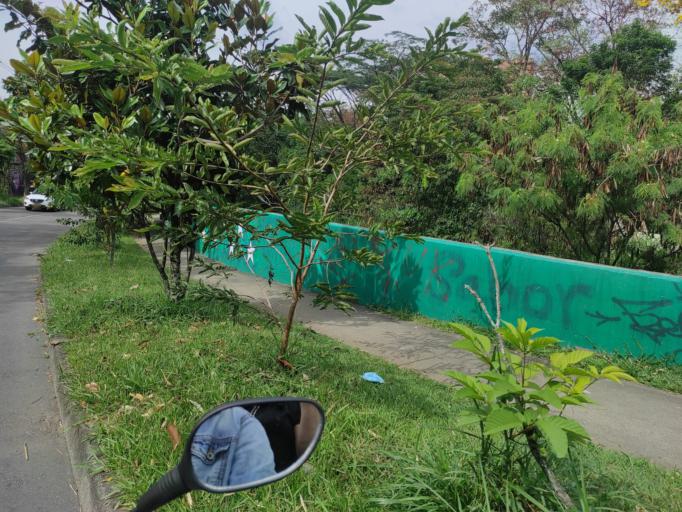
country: CO
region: Antioquia
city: Envigado
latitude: 6.1618
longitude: -75.5804
